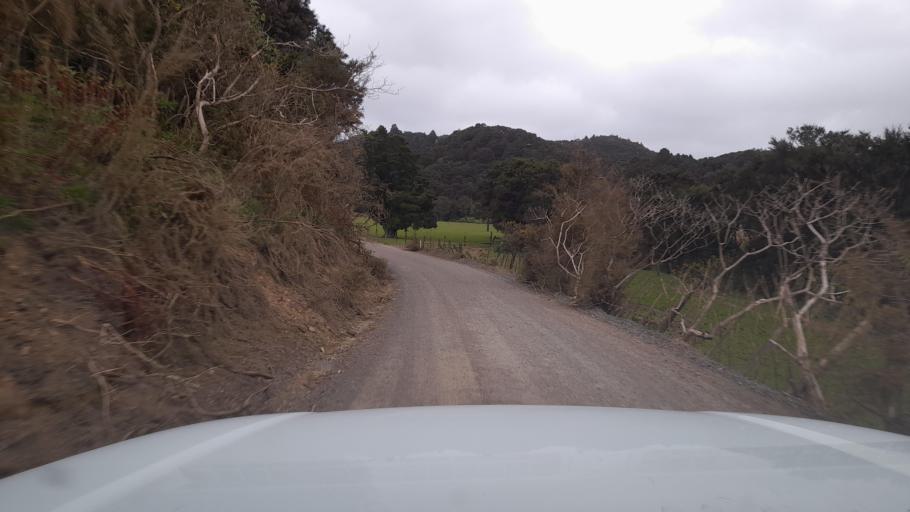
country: NZ
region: Northland
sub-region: Far North District
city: Paihia
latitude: -35.3517
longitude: 174.2263
